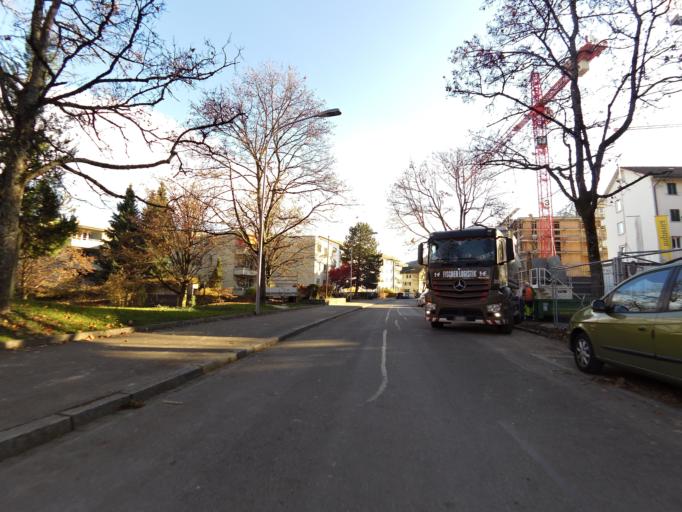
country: CH
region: Zurich
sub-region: Bezirk Zuerich
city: Zuerich (Kreis 9) / Albisrieden
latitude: 47.3726
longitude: 8.4908
